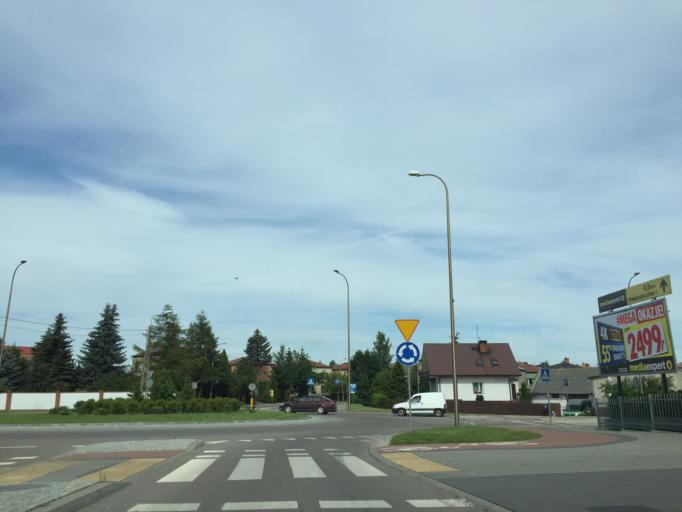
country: PL
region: Podlasie
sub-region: Suwalki
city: Suwalki
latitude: 54.0829
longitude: 22.9222
